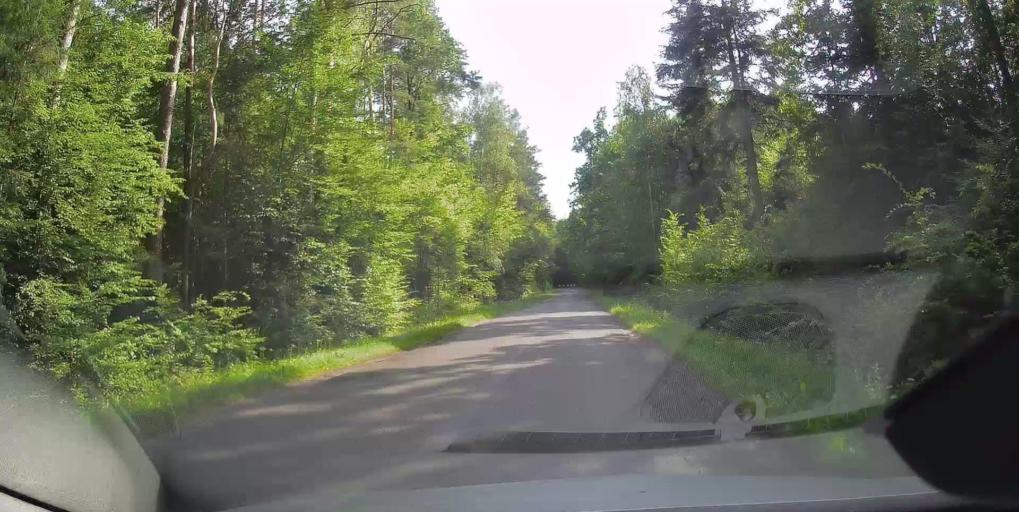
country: PL
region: Lodz Voivodeship
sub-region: Powiat opoczynski
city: Mniszkow
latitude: 51.4397
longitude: 20.0244
